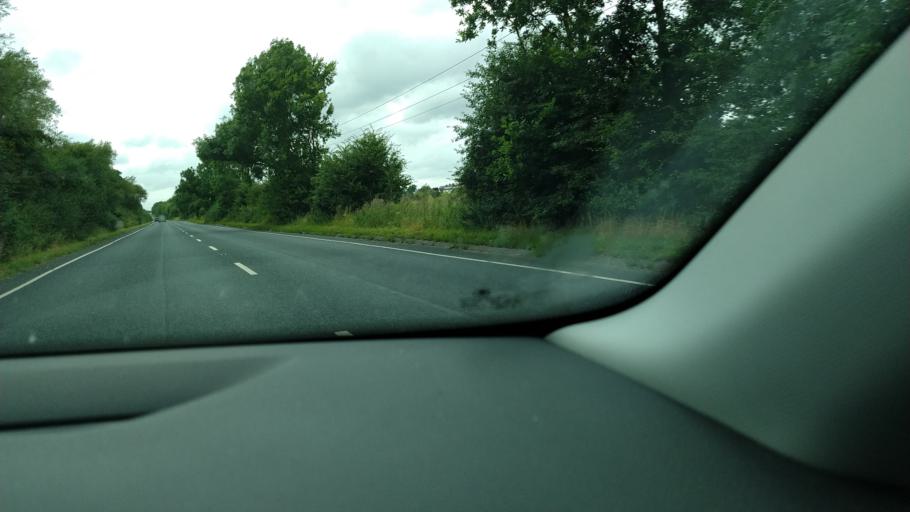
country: GB
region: England
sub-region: East Riding of Yorkshire
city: Rawcliffe
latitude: 53.7104
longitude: -0.9469
